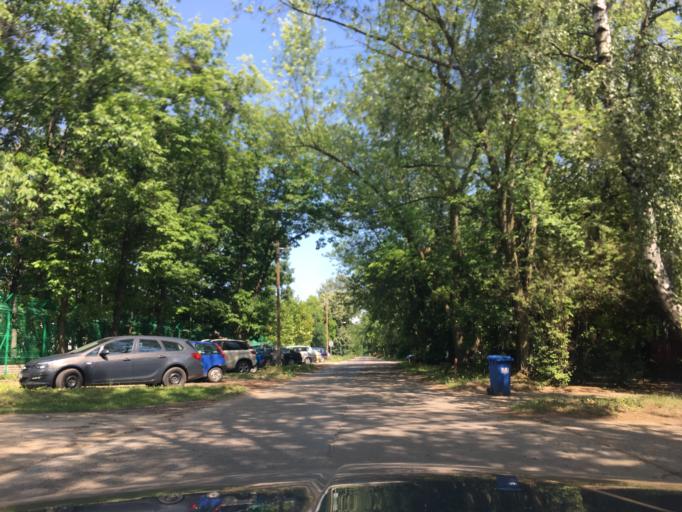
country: HU
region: Hajdu-Bihar
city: Debrecen
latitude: 47.5612
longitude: 21.6327
